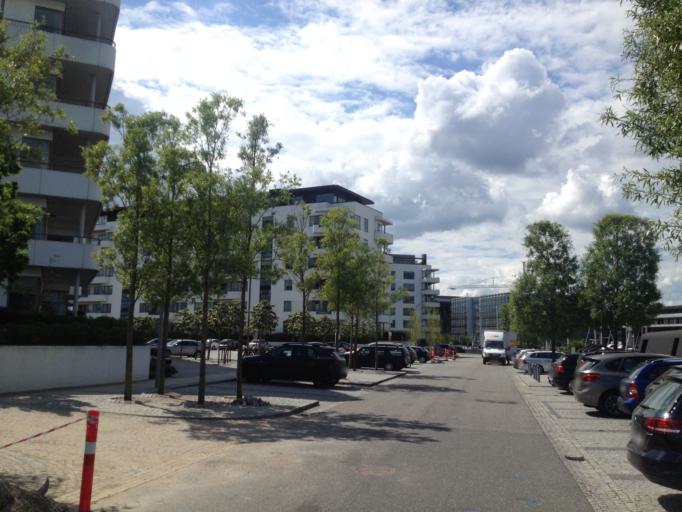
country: DK
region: Capital Region
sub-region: Gentofte Kommune
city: Charlottenlund
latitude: 55.7255
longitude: 12.5875
